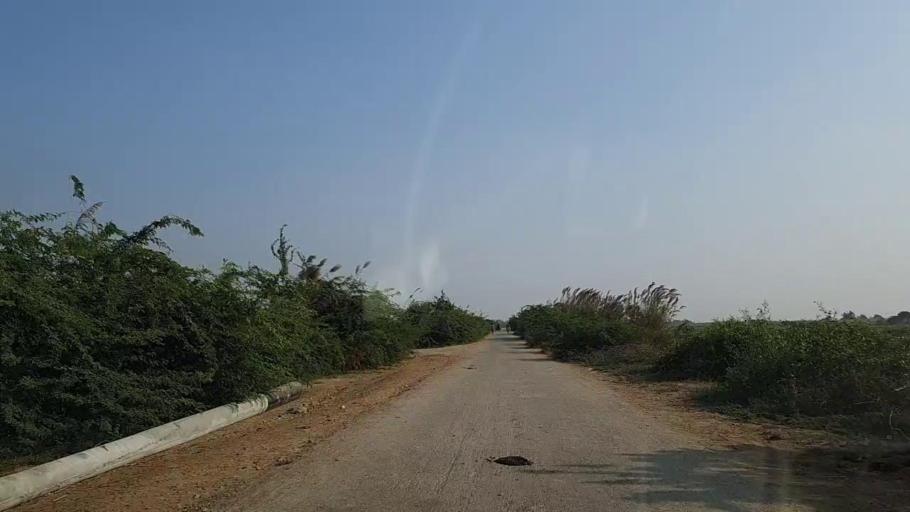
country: PK
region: Sindh
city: Mirpur Sakro
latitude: 24.6258
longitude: 67.6544
